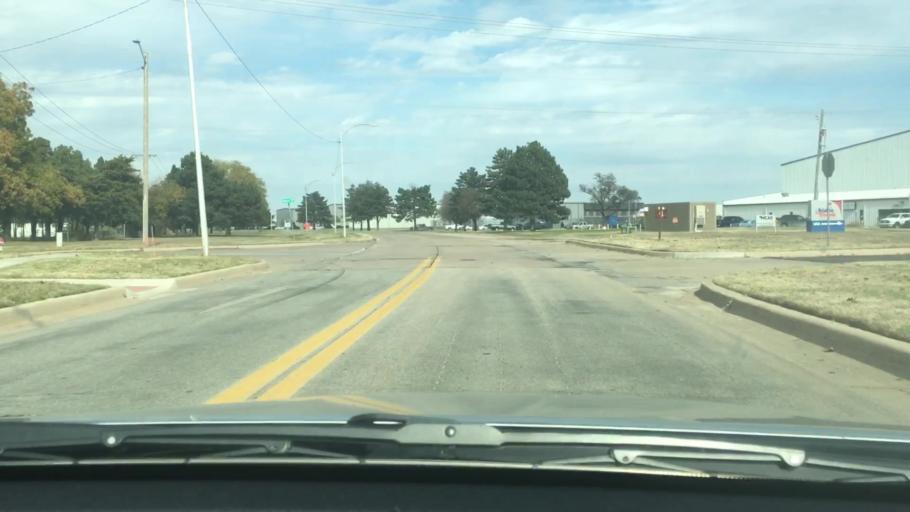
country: US
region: Kansas
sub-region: Sedgwick County
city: Wichita
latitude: 37.6650
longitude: -97.4216
